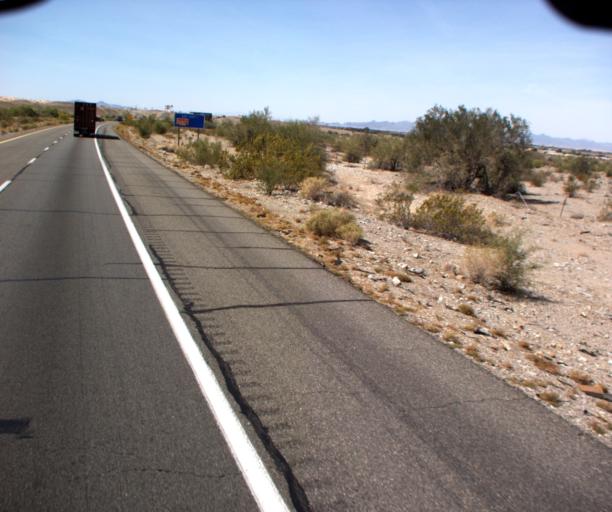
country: US
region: Arizona
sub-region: La Paz County
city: Ehrenberg
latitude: 33.6039
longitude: -114.5056
